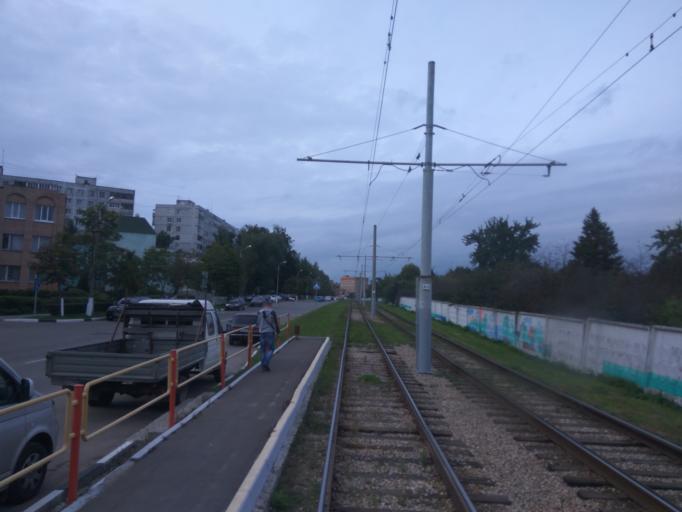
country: RU
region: Moskovskaya
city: Kolomna
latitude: 55.0612
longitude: 38.7577
